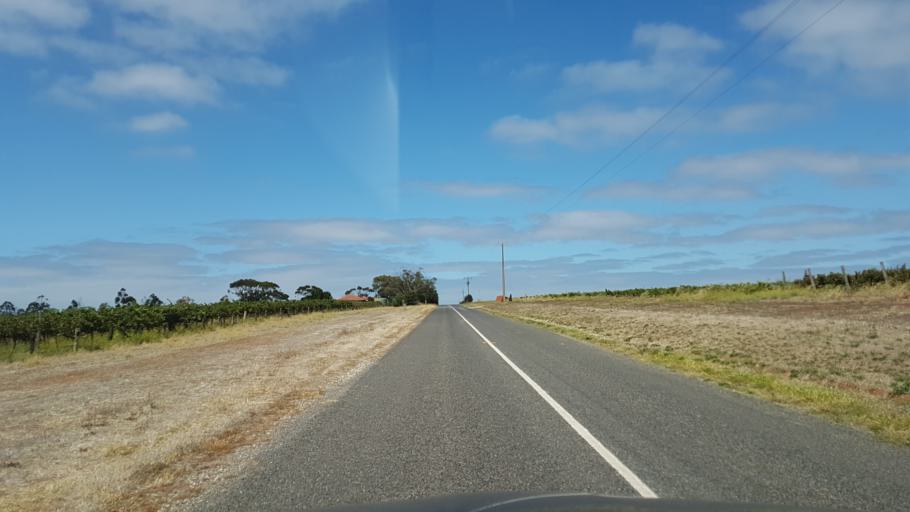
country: AU
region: South Australia
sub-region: Onkaparinga
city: McLaren Vale
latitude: -35.2118
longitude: 138.5175
